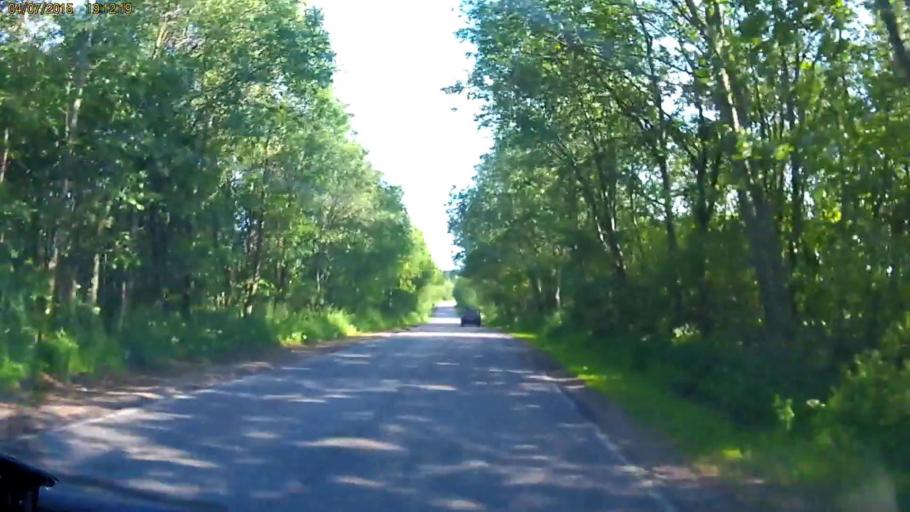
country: RU
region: Leningrad
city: Garbolovo
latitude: 60.3184
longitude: 30.4934
